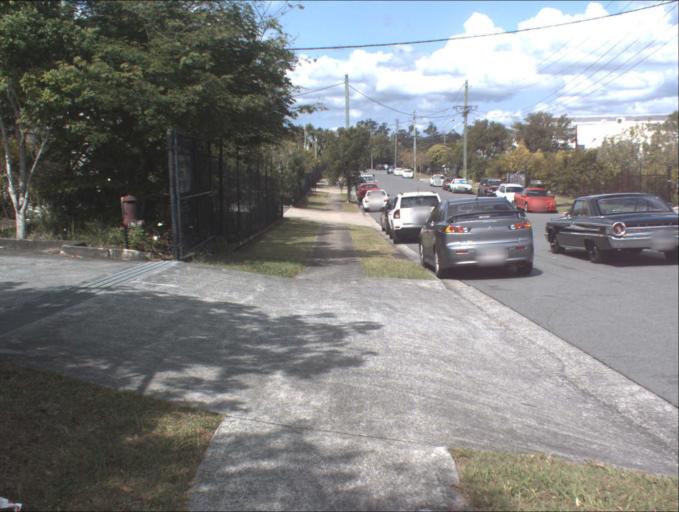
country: AU
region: Queensland
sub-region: Logan
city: Waterford West
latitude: -27.6670
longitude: 153.1334
